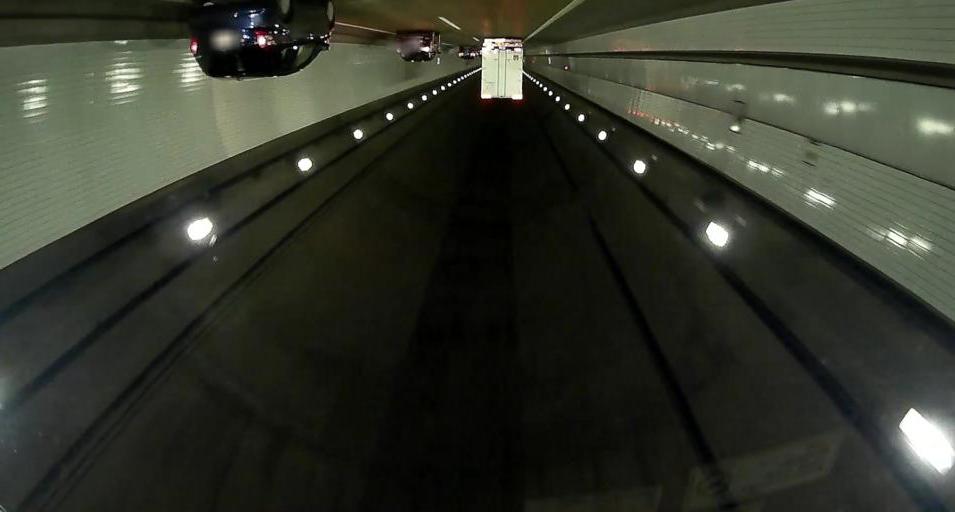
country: JP
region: Chiba
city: Kisarazu
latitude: 35.4720
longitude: 139.8626
